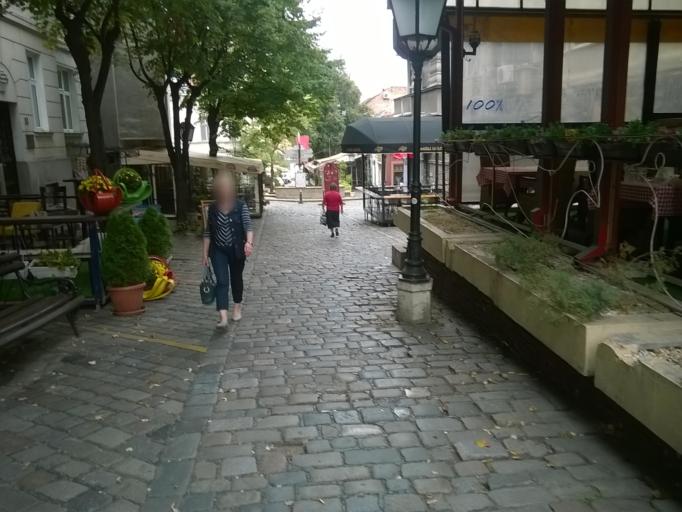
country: RS
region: Central Serbia
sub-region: Belgrade
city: Stari Grad
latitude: 44.8166
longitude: 20.4636
